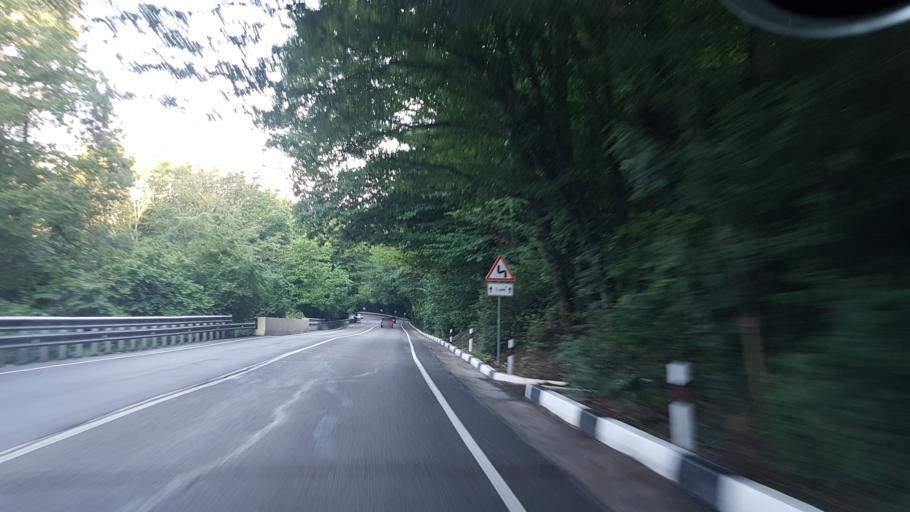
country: RU
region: Krasnodarskiy
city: Gornoye Loo
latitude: 43.6760
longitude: 39.6128
